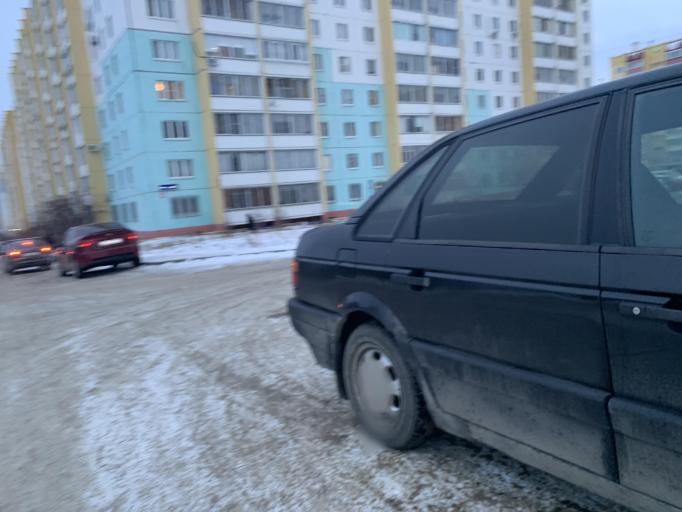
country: RU
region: Chelyabinsk
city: Roshchino
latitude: 55.1905
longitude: 61.2722
